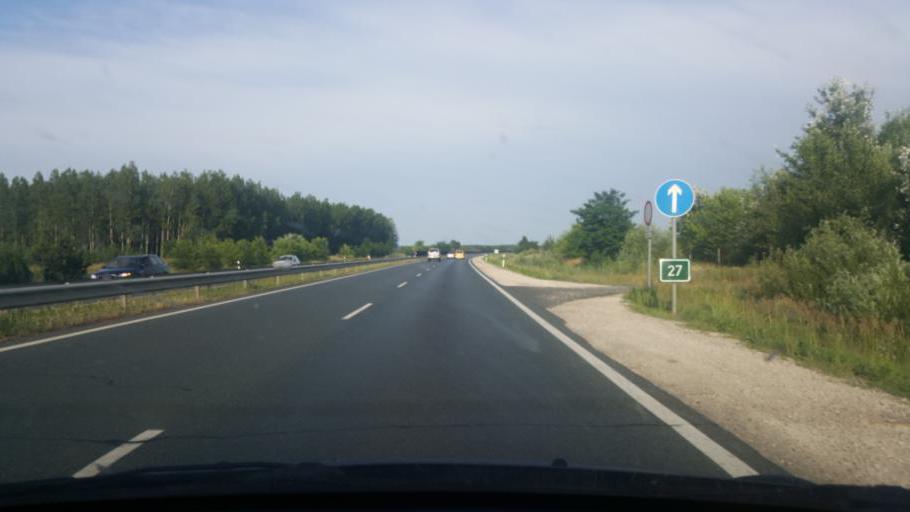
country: HU
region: Pest
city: Ullo
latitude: 47.4035
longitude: 19.3419
